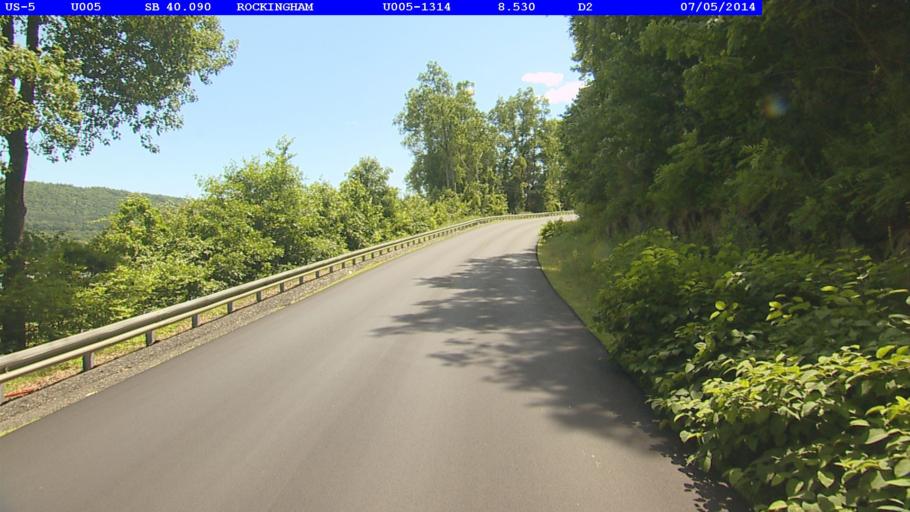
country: US
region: New Hampshire
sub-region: Sullivan County
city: Charlestown
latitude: 43.2286
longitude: -72.4373
